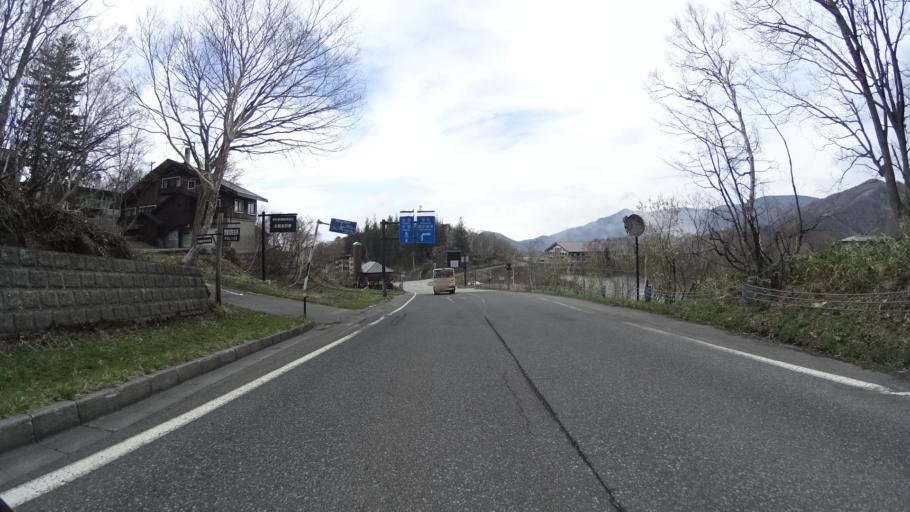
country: JP
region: Nagano
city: Nakano
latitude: 36.7168
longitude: 138.4933
